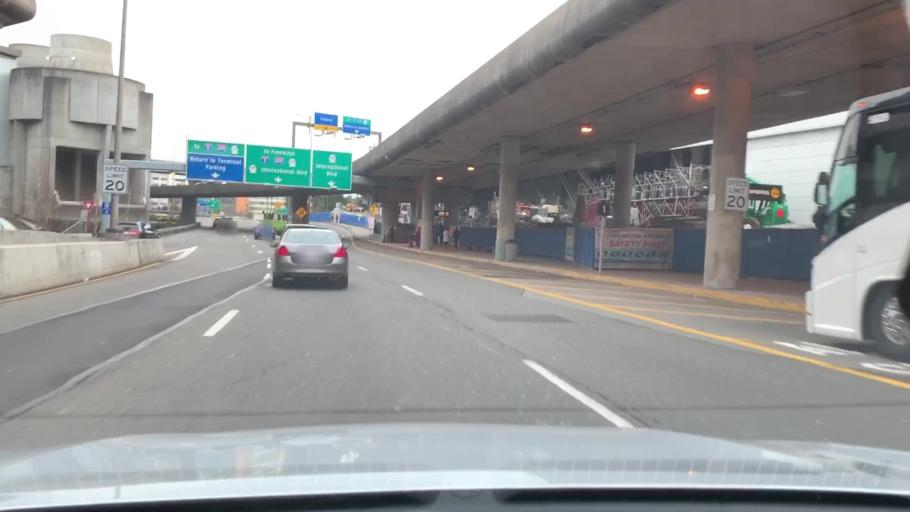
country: US
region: Washington
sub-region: King County
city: SeaTac
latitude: 47.4417
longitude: -122.2990
